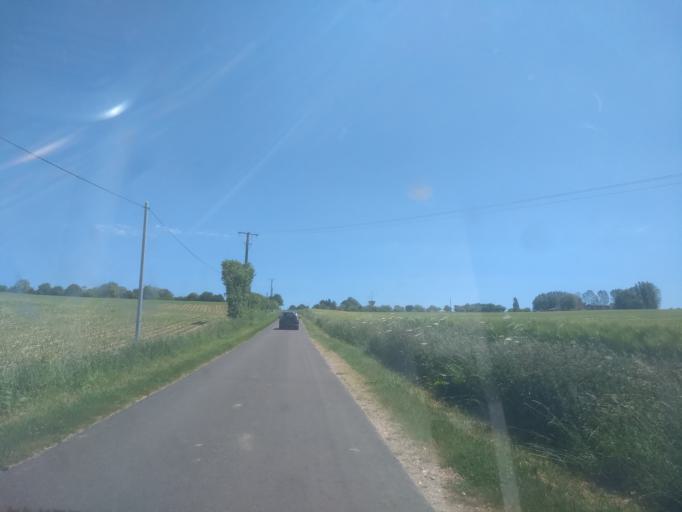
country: FR
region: Lower Normandy
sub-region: Departement de l'Orne
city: Belleme
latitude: 48.4081
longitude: 0.6339
